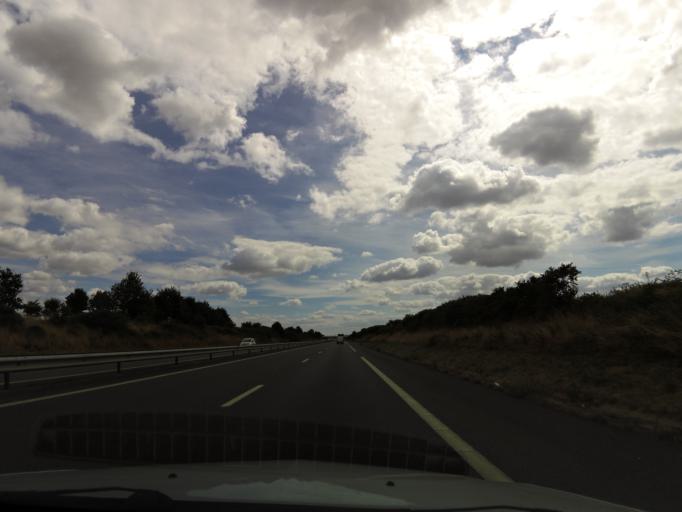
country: FR
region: Pays de la Loire
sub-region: Departement de la Loire-Atlantique
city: La Planche
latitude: 46.9995
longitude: -1.3841
